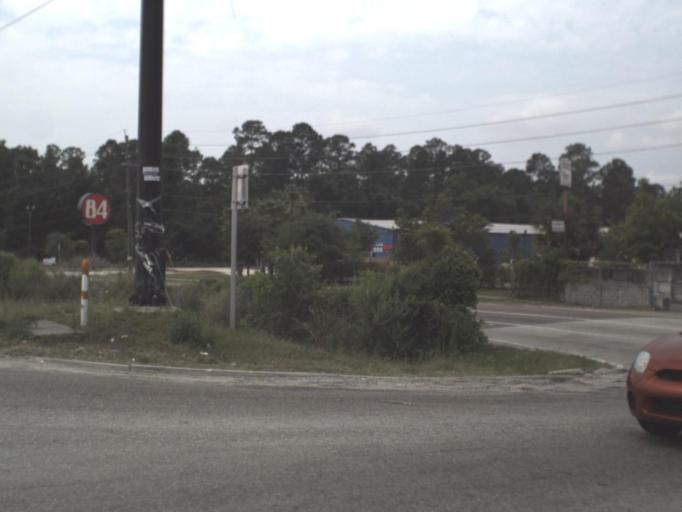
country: US
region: Florida
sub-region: Clay County
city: Orange Park
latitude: 30.1961
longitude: -81.7076
